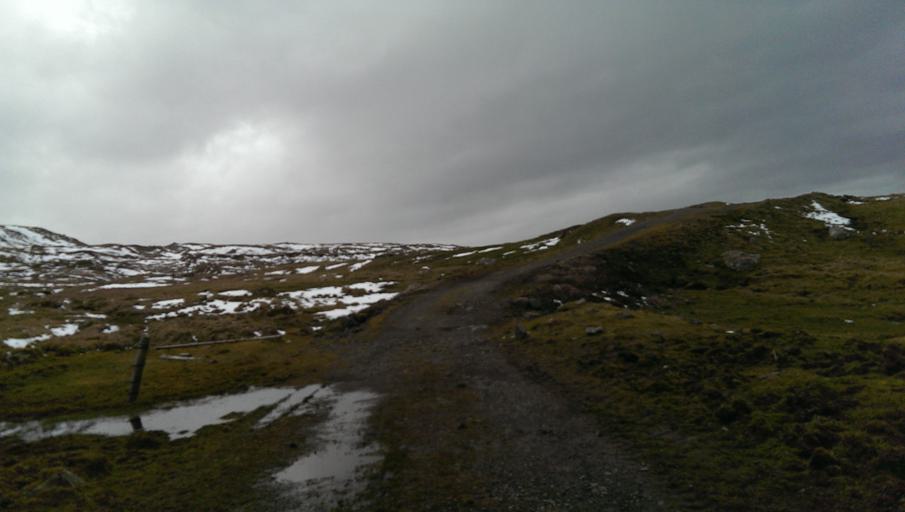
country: FO
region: Streymoy
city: Hoyvik
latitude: 62.0335
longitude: -6.8058
